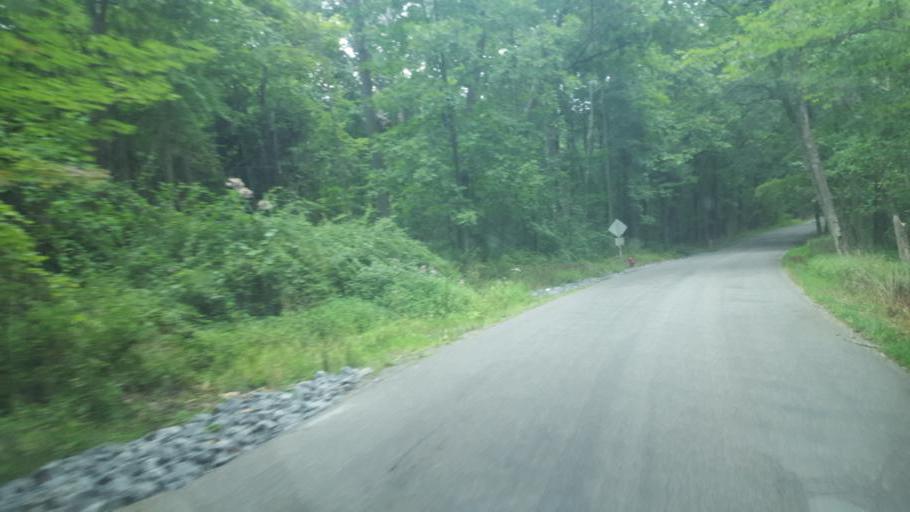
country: US
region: Pennsylvania
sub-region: Clarion County
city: Marianne
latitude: 41.2043
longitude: -79.4340
